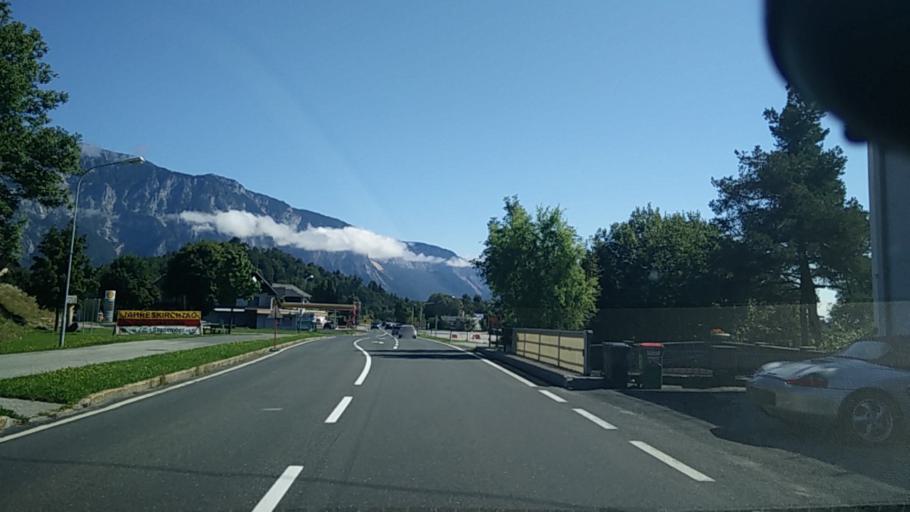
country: AT
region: Carinthia
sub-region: Politischer Bezirk Villach Land
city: Hohenthurn
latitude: 46.5432
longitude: 13.6522
